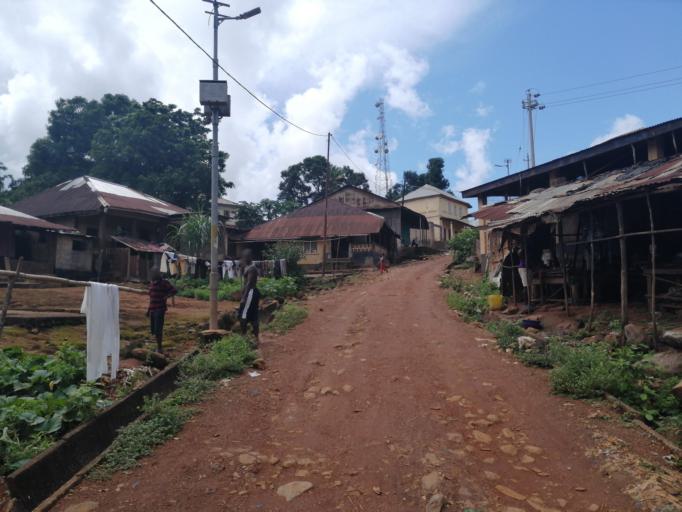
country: SL
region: Northern Province
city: Port Loko
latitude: 8.7642
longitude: -12.7907
